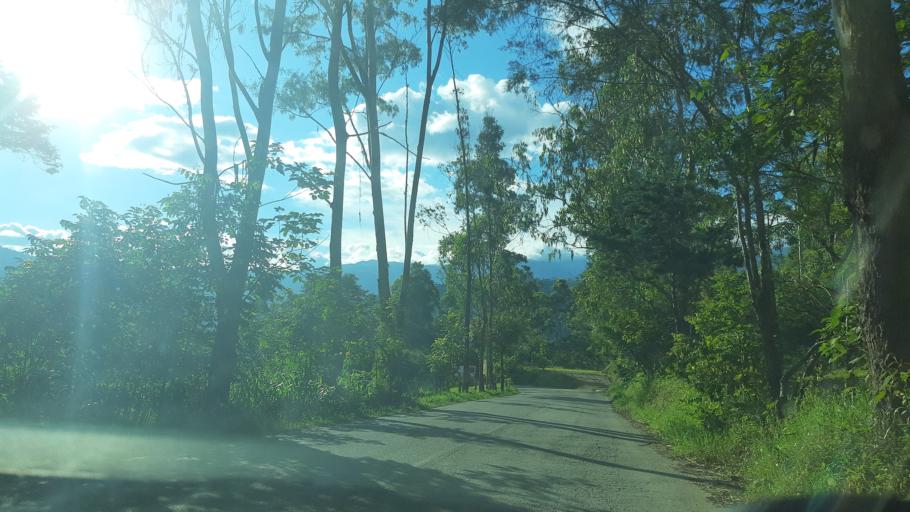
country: CO
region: Boyaca
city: Garagoa
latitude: 5.0742
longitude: -73.3770
